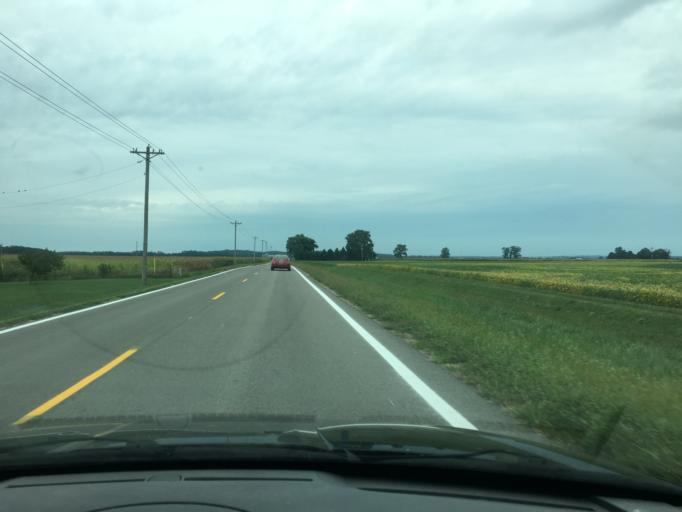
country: US
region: Ohio
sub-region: Logan County
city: West Liberty
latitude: 40.1904
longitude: -83.7814
